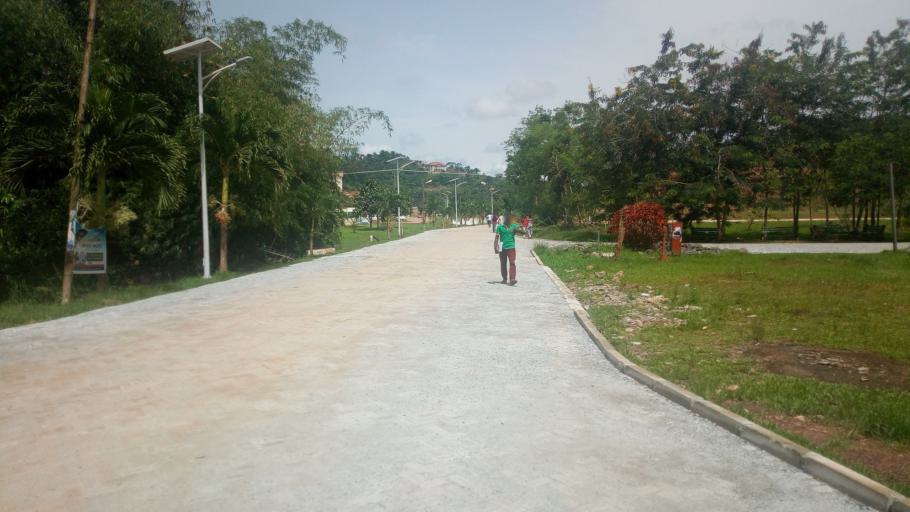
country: GH
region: Western
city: Tarkwa
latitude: 5.2990
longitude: -2.0033
